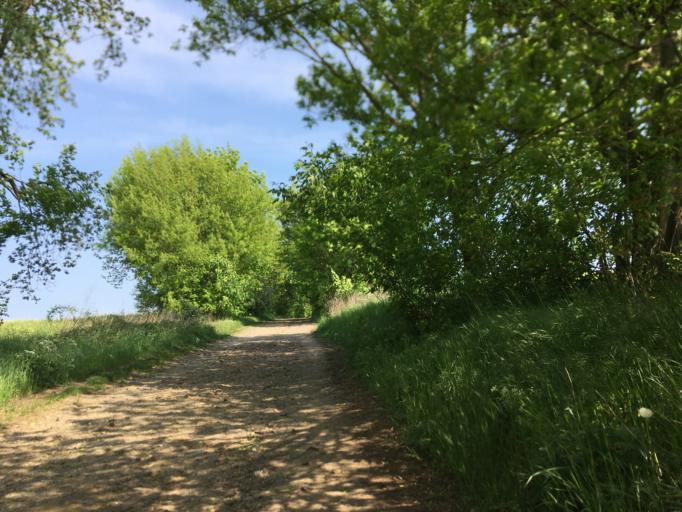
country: DE
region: Brandenburg
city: Altlandsberg
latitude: 52.5856
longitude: 13.7261
